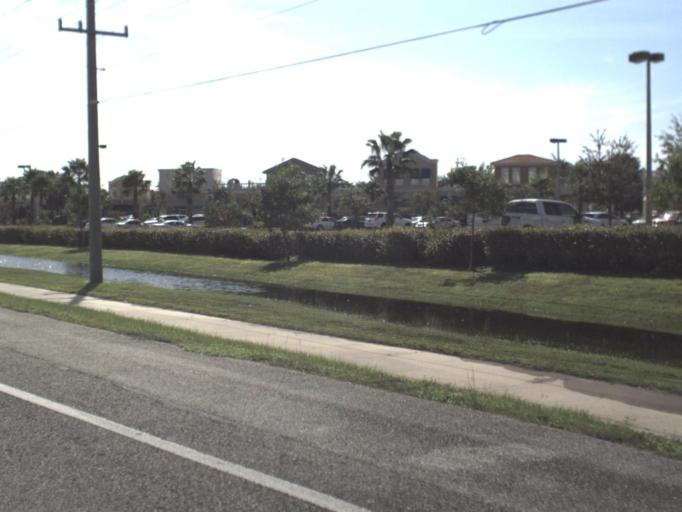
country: US
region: Florida
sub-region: Sarasota County
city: North Port
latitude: 27.0403
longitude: -82.2265
